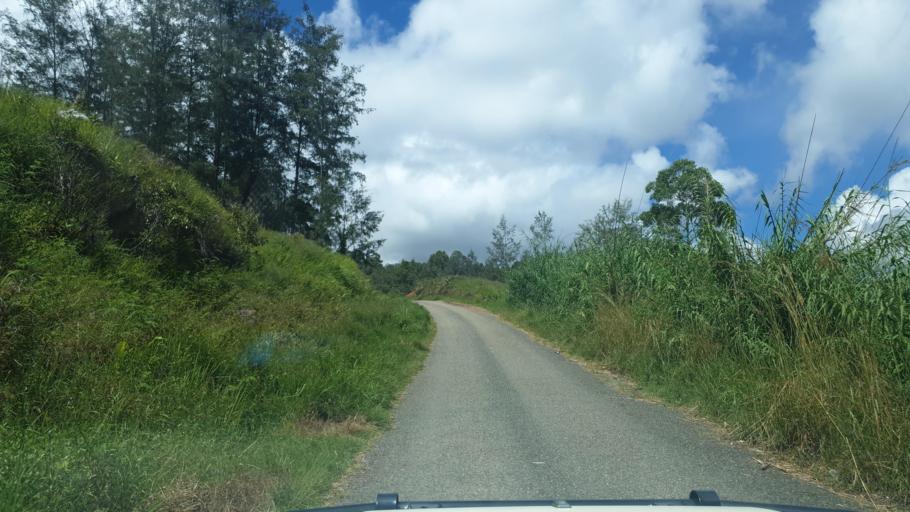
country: PG
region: Chimbu
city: Kundiawa
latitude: -6.1545
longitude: 145.1337
